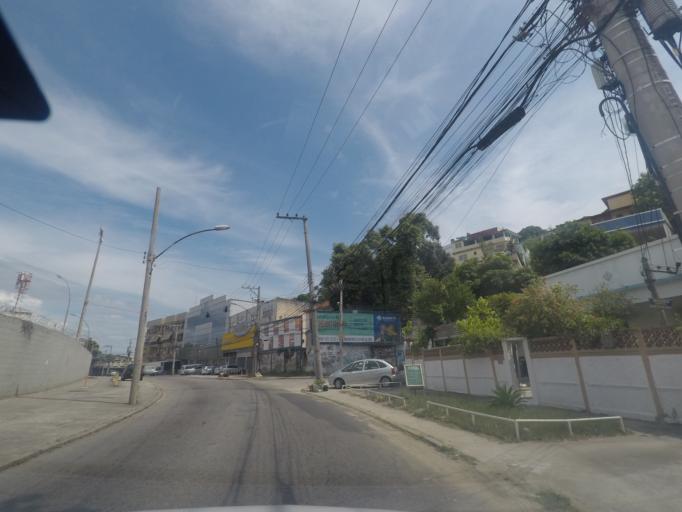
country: BR
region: Rio de Janeiro
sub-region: Rio De Janeiro
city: Rio de Janeiro
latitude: -22.8159
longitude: -43.1887
